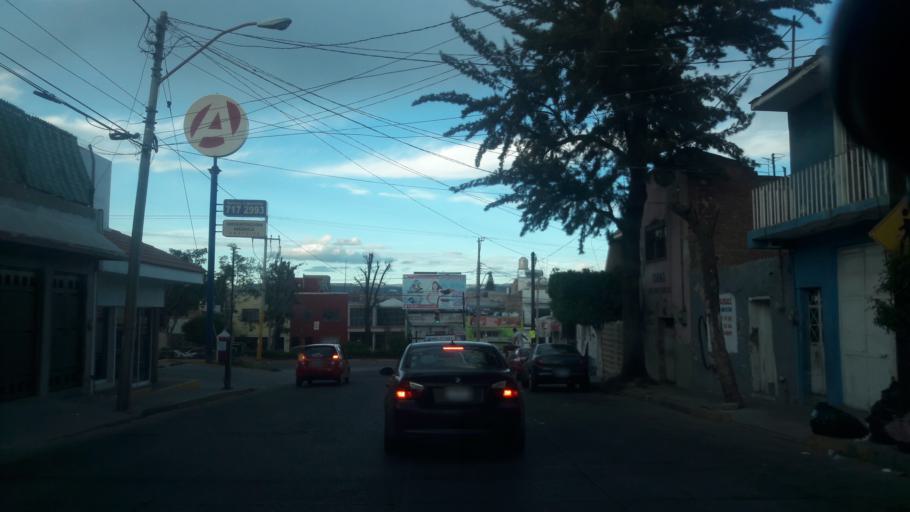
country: MX
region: Guanajuato
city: Leon
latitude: 21.1298
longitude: -101.6920
